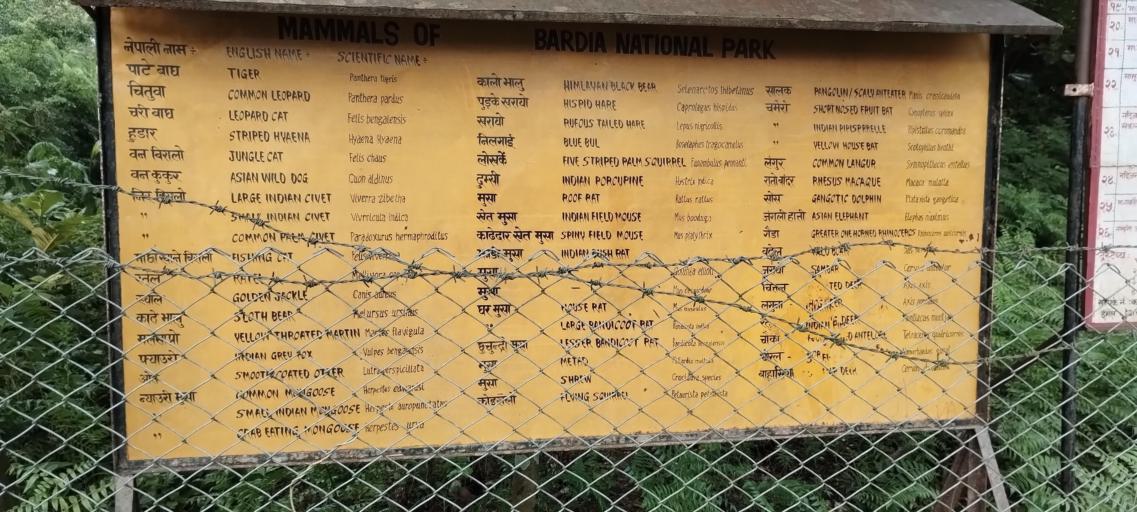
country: NP
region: Far Western
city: Tikapur
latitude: 28.4519
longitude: 81.2431
